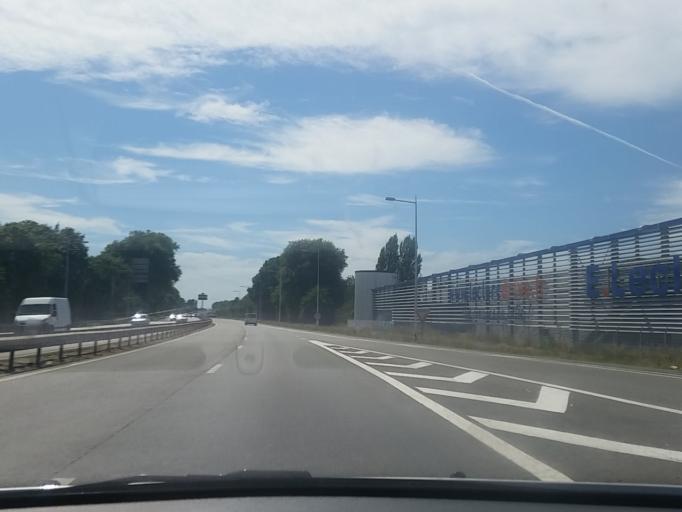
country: FR
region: Pays de la Loire
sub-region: Departement de la Loire-Atlantique
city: Reze
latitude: 47.1925
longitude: -1.5732
